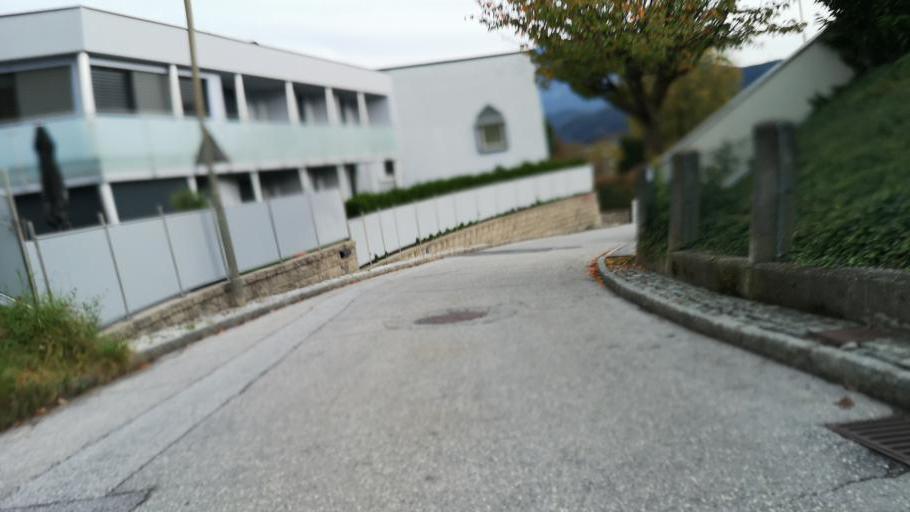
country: AT
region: Tyrol
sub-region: Politischer Bezirk Innsbruck Land
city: Vols
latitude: 47.2691
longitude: 11.3547
